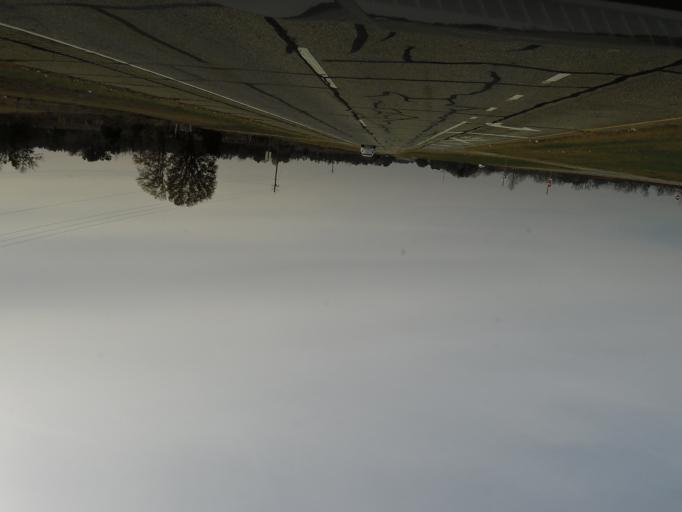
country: US
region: Georgia
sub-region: Seminole County
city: Donalsonville
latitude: 31.0699
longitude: -84.9482
